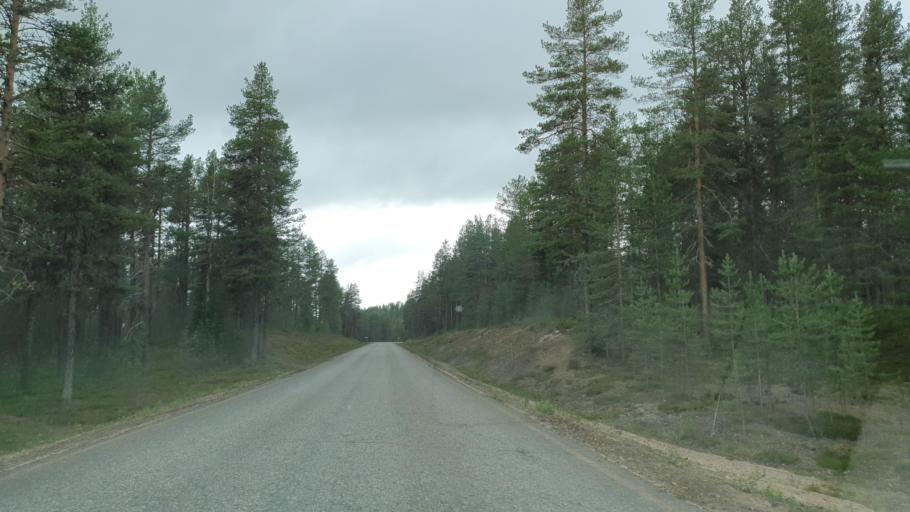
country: FI
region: Lapland
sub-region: Tunturi-Lappi
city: Kolari
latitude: 67.5392
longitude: 23.9555
